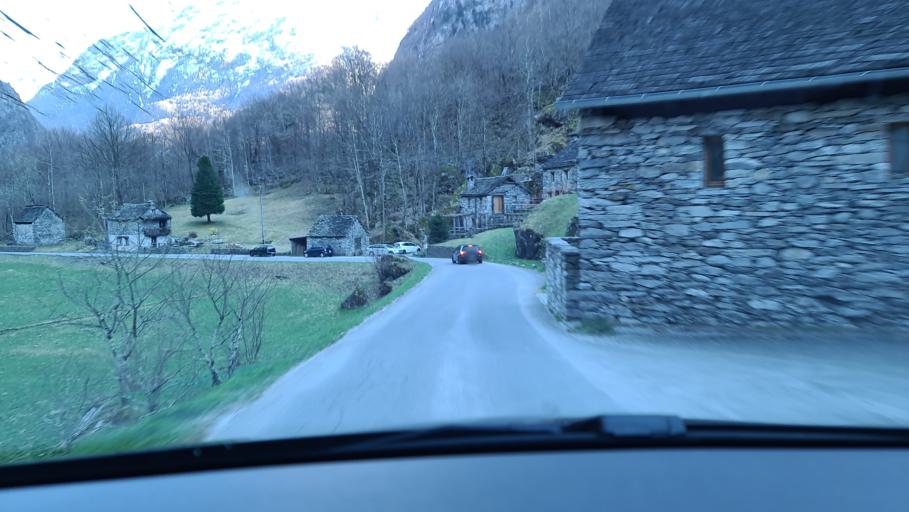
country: CH
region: Ticino
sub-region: Vallemaggia District
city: Cevio
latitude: 46.3943
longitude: 8.5380
